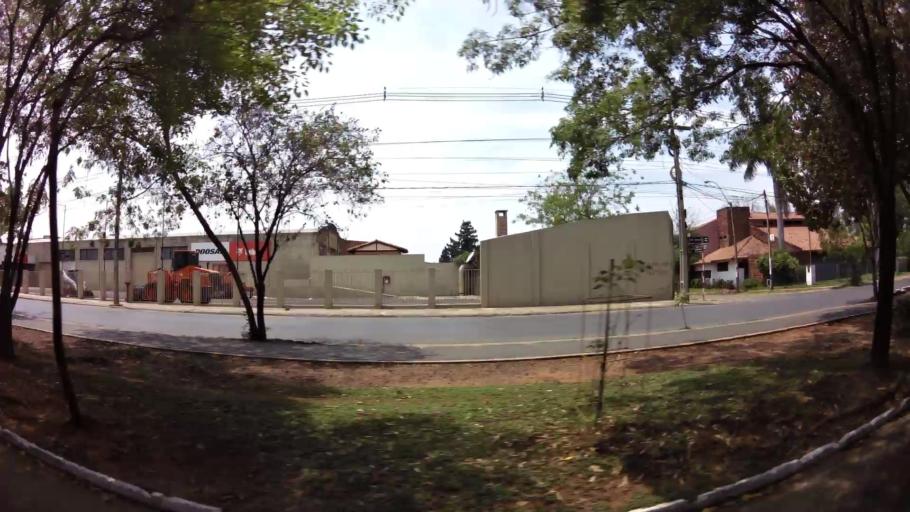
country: PY
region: Central
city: Fernando de la Mora
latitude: -25.3112
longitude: -57.5655
